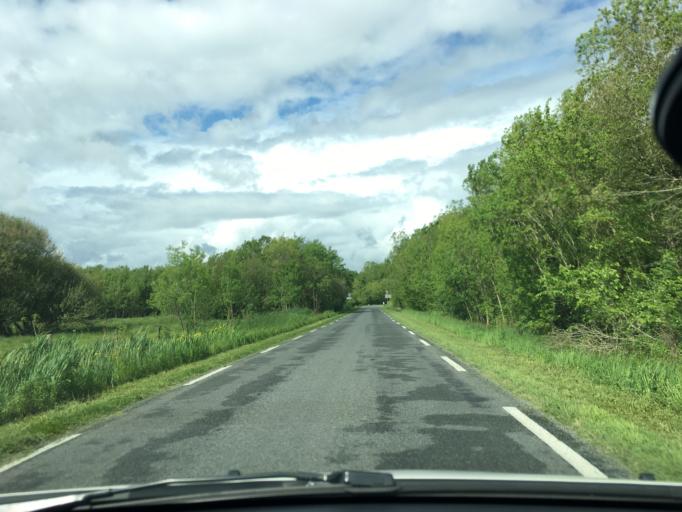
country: FR
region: Aquitaine
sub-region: Departement de la Gironde
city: Saint-Estephe
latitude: 45.3202
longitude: -0.8128
